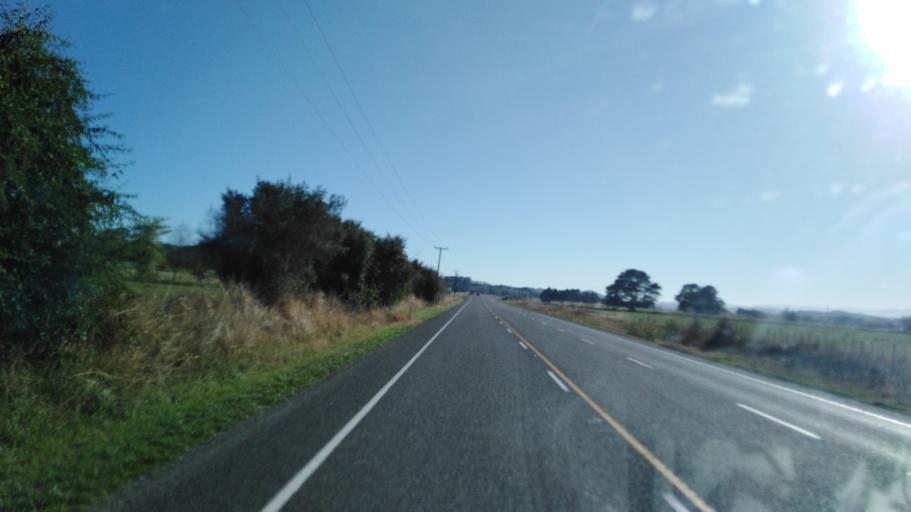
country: NZ
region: Manawatu-Wanganui
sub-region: Rangitikei District
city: Bulls
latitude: -39.9087
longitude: 175.6396
